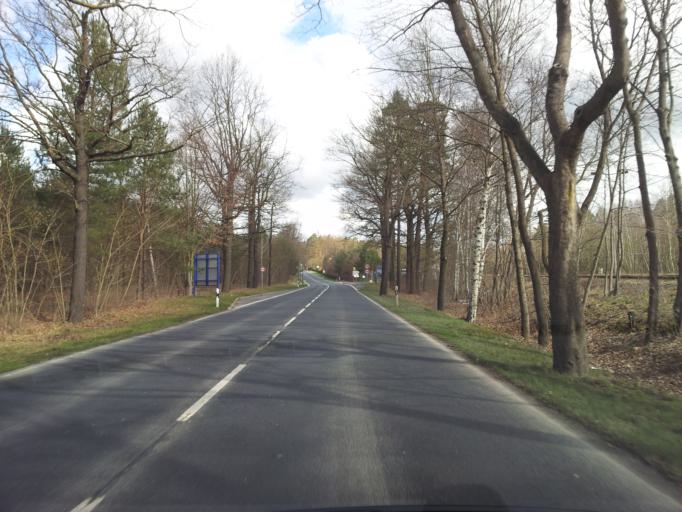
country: DE
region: Saxony
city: Ottendorf-Okrilla
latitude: 51.2054
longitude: 13.8374
